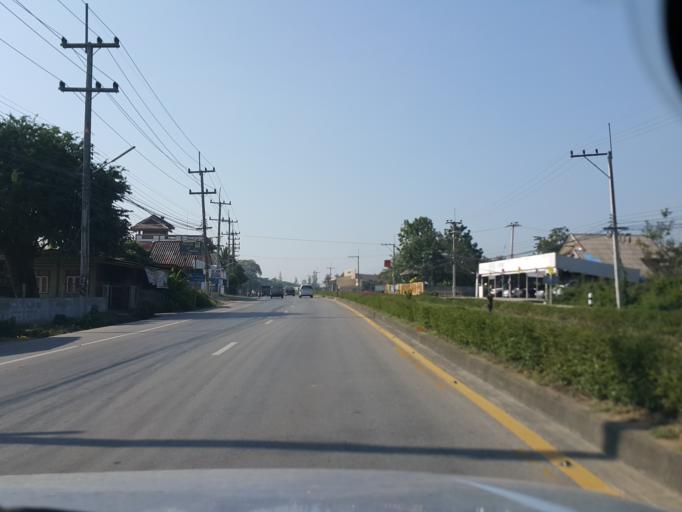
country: TH
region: Chiang Mai
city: San Pa Tong
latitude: 18.5870
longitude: 98.8867
